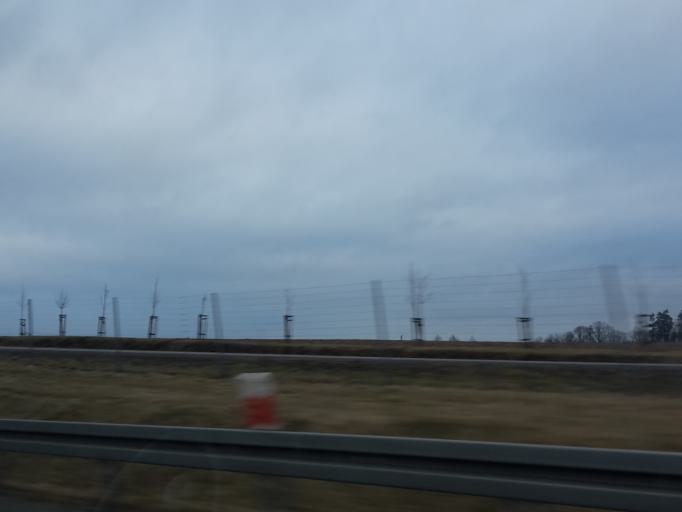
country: PL
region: Warmian-Masurian Voivodeship
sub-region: Powiat ostrodzki
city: Maldyty
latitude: 53.8694
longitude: 19.7423
